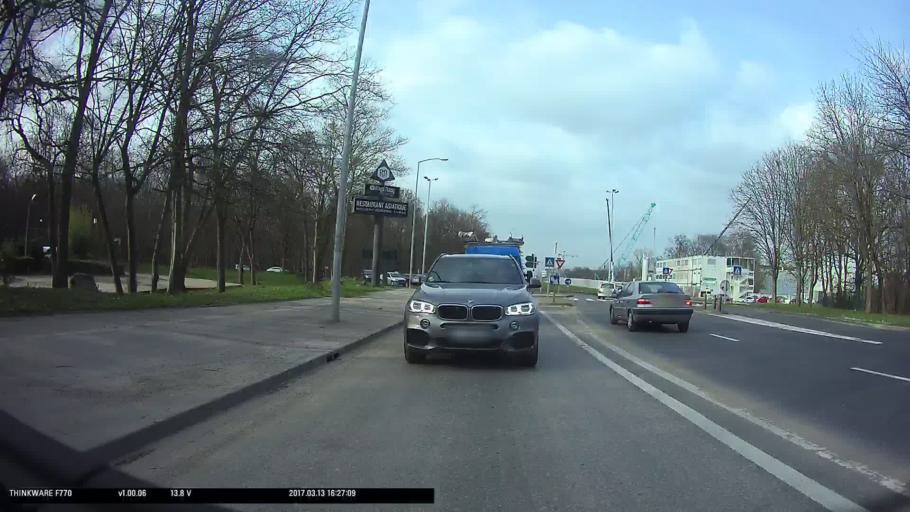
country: FR
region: Ile-de-France
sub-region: Departement de Seine-et-Marne
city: Champs-sur-Marne
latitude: 48.8372
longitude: 2.5822
